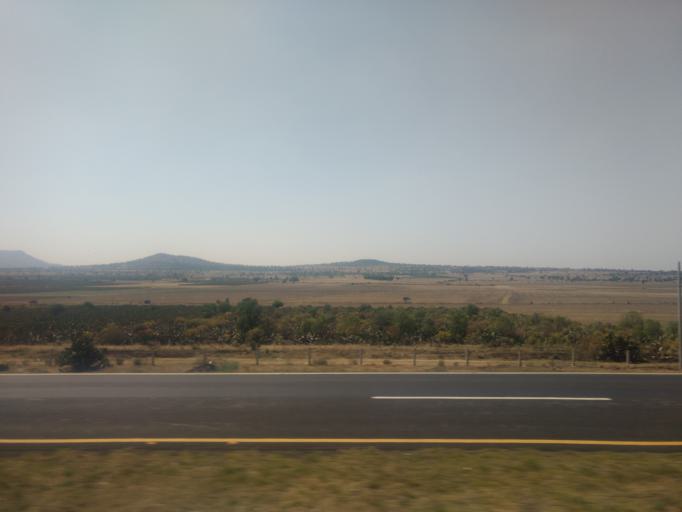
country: MX
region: Morelos
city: Nopaltepec
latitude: 19.8030
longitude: -98.7240
